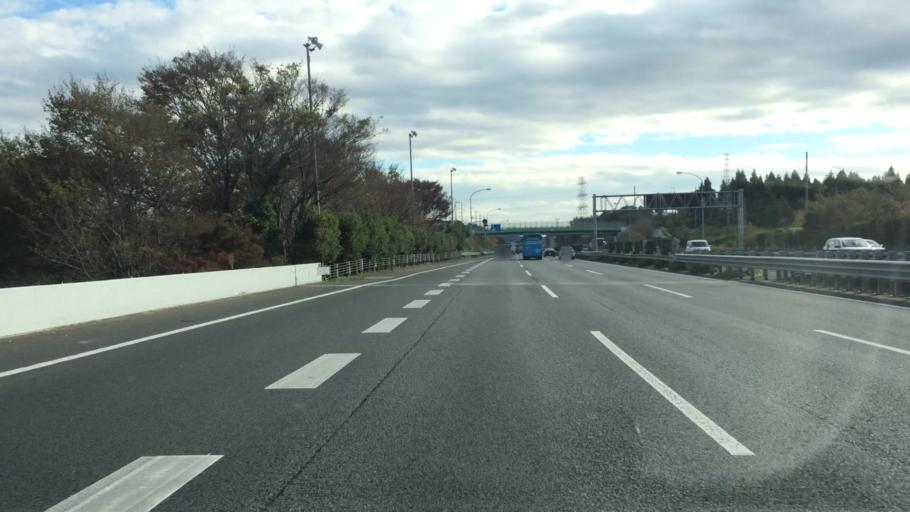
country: JP
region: Chiba
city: Yotsukaido
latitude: 35.6842
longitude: 140.1845
